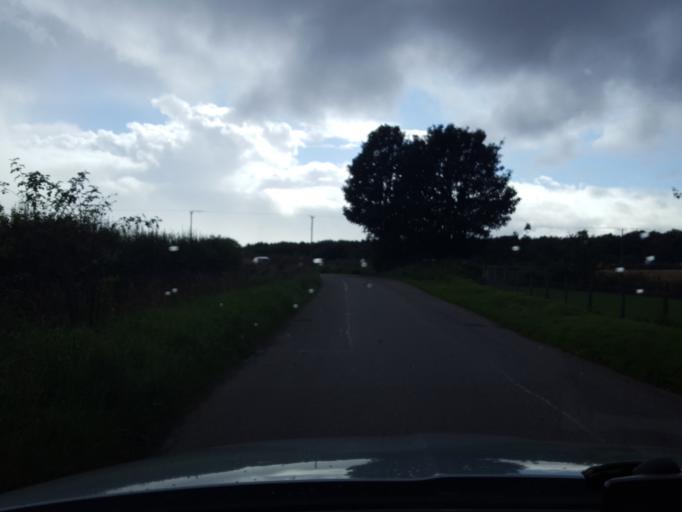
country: GB
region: Scotland
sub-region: Aberdeenshire
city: Banchory
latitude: 57.0901
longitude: -2.4475
